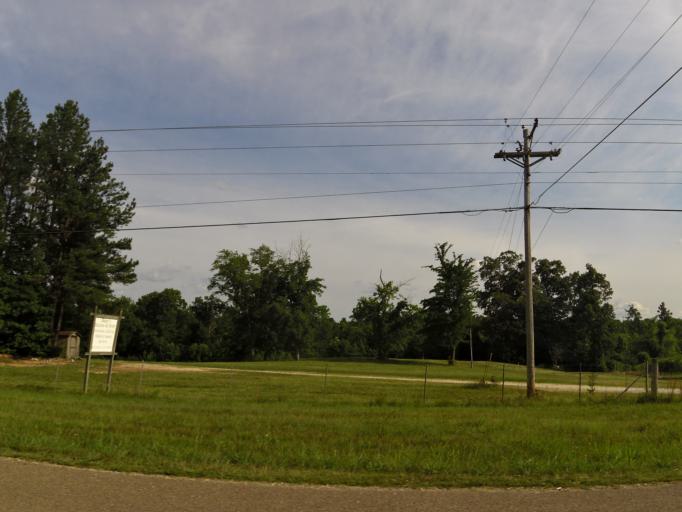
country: US
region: Tennessee
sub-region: Benton County
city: Camden
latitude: 36.0454
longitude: -88.1428
